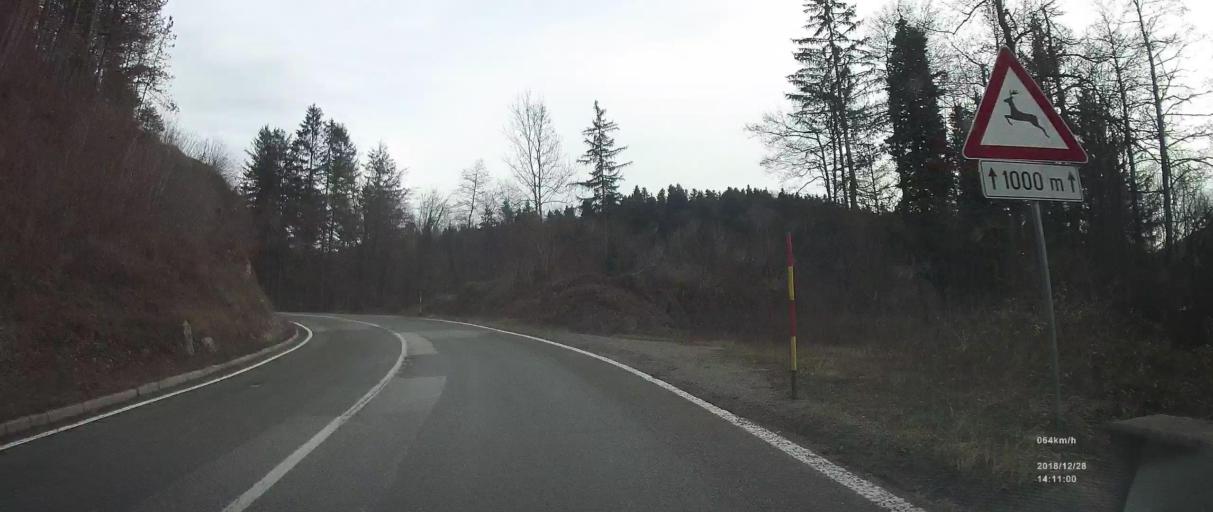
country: SI
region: Kostel
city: Kostel
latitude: 45.4497
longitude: 14.9805
